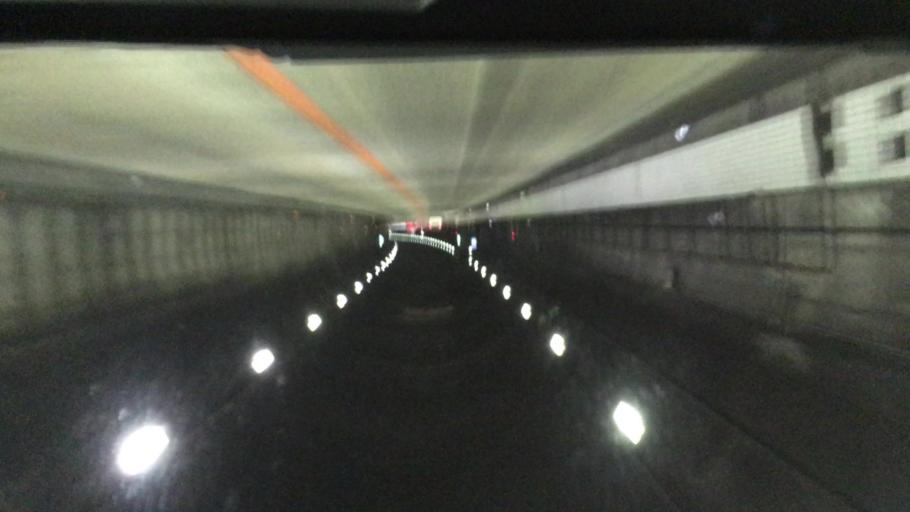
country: JP
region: Yamaguchi
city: Tokuyama
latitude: 34.0853
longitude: 131.7447
